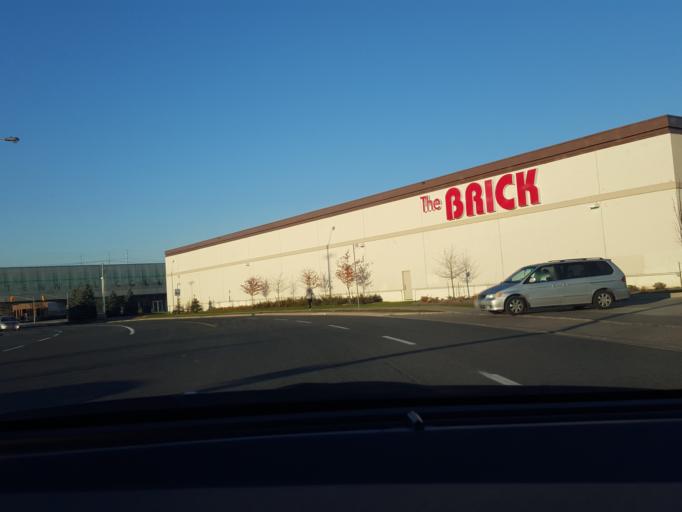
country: CA
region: Ontario
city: Scarborough
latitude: 43.7285
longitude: -79.2917
